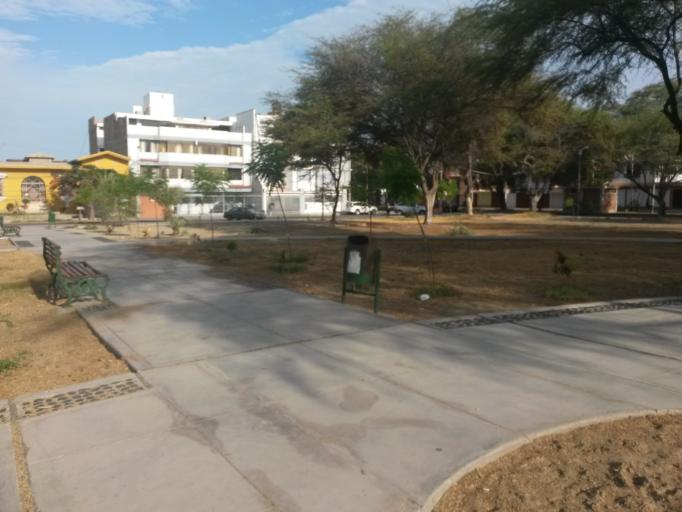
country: PE
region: Piura
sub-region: Provincia de Piura
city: Piura
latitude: -5.1729
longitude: -80.6280
